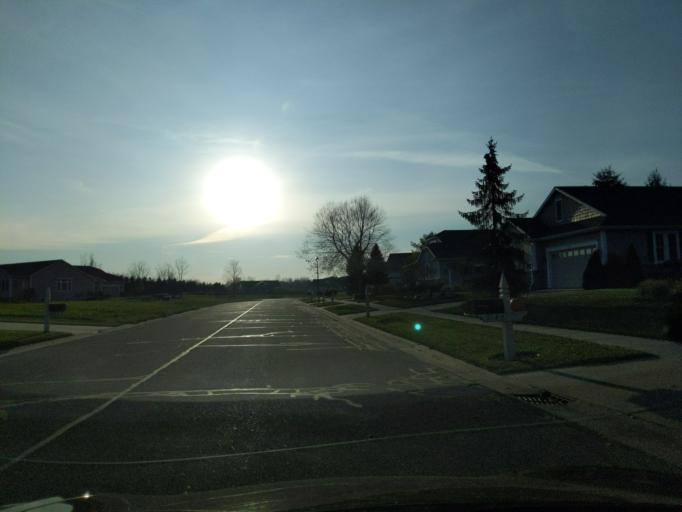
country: US
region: Michigan
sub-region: Clinton County
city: Bath
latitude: 42.7951
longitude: -84.4595
